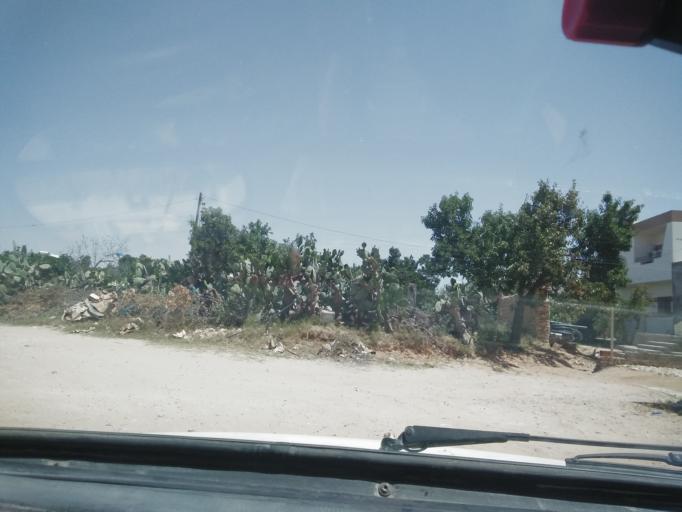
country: TN
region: Safaqis
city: Al Qarmadah
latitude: 34.8043
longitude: 10.7762
